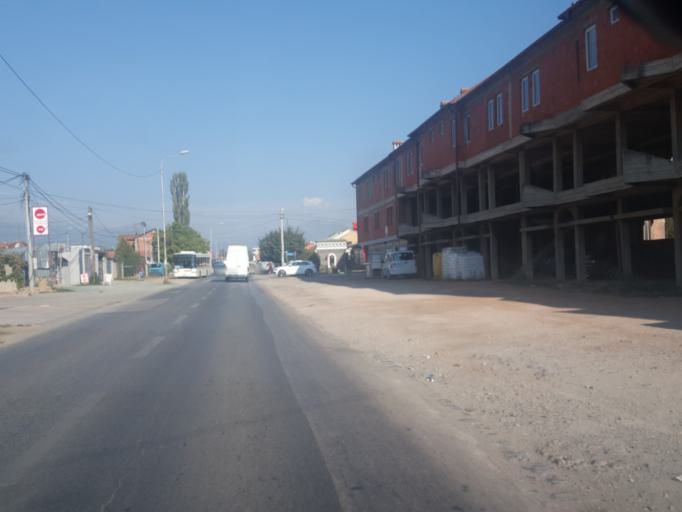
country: XK
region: Gjakova
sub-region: Komuna e Gjakoves
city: Gjakove
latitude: 42.4008
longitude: 20.4153
